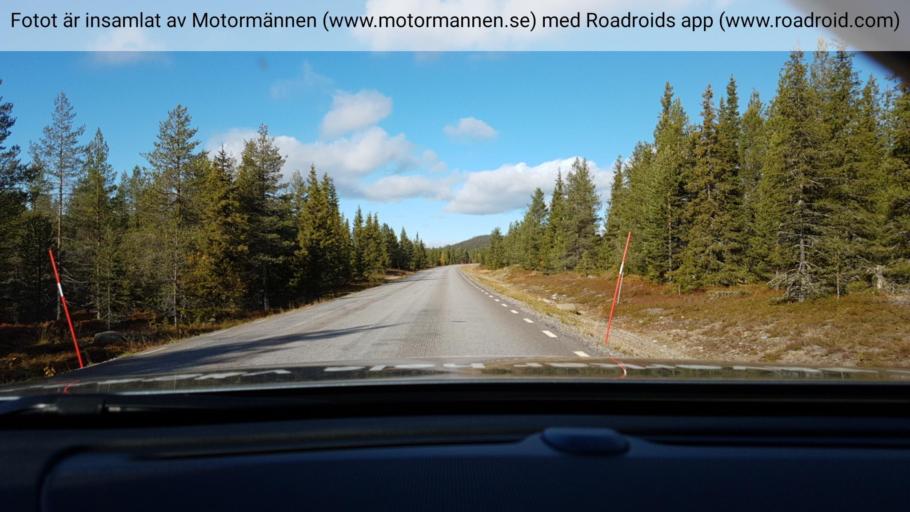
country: SE
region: Norrbotten
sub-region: Arjeplogs Kommun
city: Arjeplog
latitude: 65.8896
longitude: 18.3775
